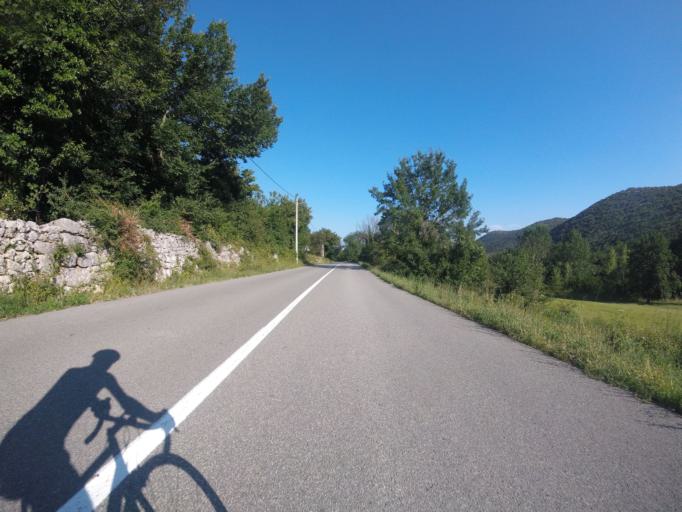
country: HR
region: Primorsko-Goranska
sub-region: Grad Crikvenica
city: Jadranovo
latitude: 45.2559
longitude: 14.6177
